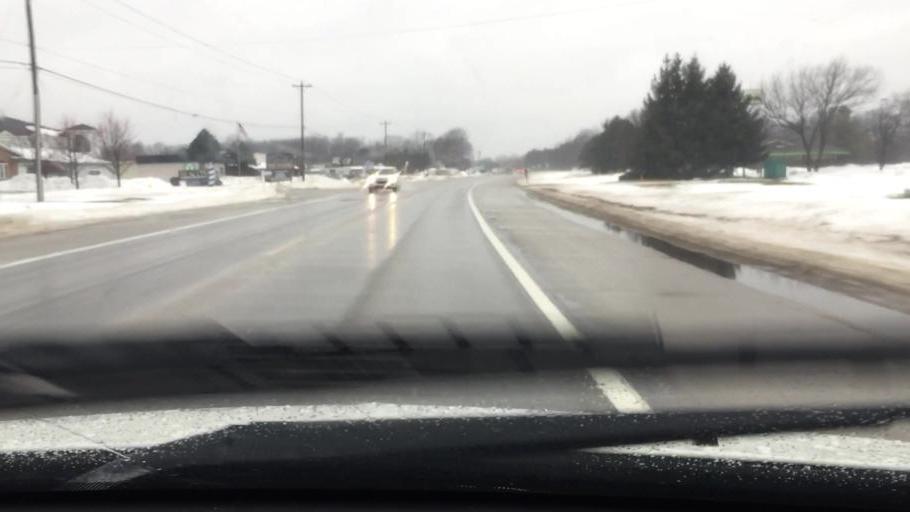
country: US
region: Michigan
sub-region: Charlevoix County
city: Charlevoix
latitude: 45.2968
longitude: -85.2546
